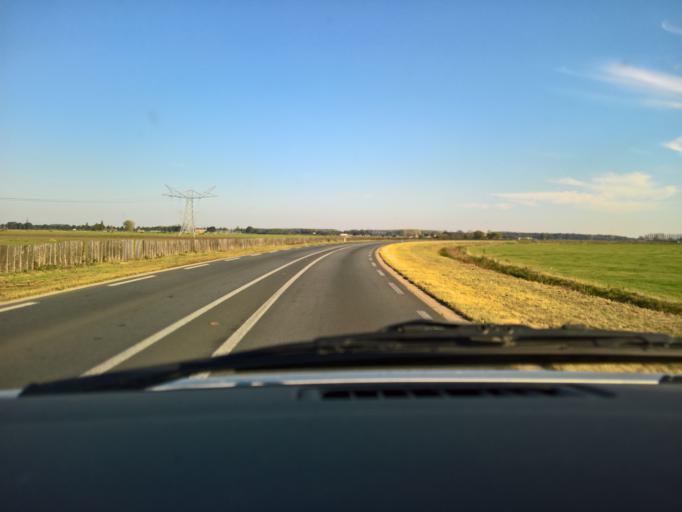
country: NL
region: Gelderland
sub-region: Gemeente Druten
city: Druten
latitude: 51.8700
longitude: 5.5643
